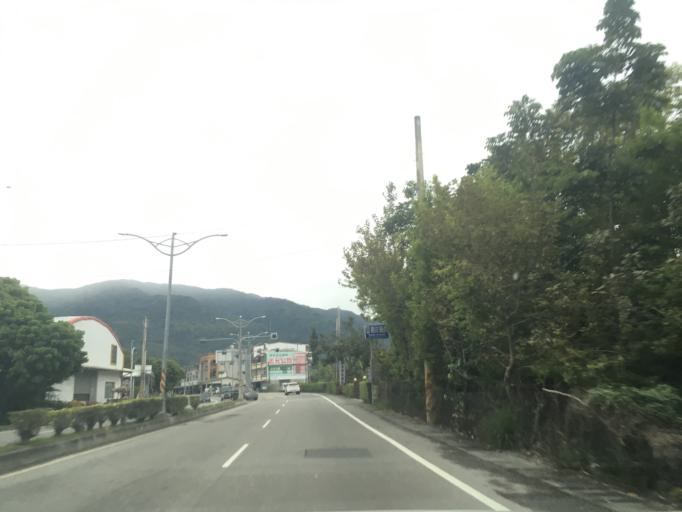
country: TW
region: Taiwan
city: Taitung City
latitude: 22.6937
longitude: 121.0459
